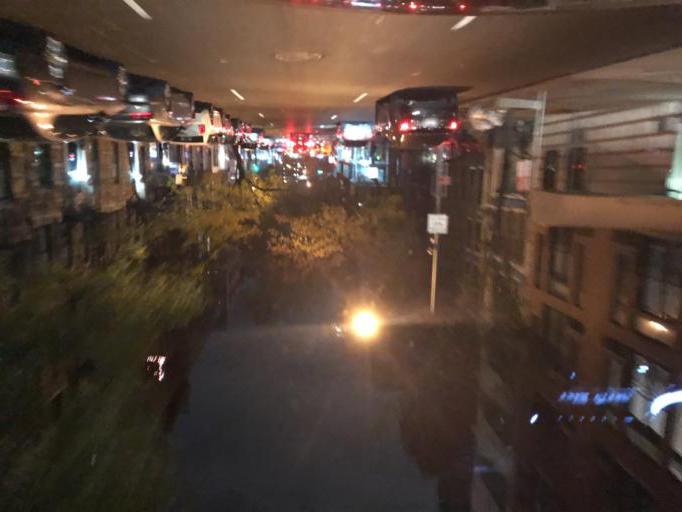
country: US
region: New York
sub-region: Queens County
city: Long Island City
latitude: 40.7620
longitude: -73.9618
